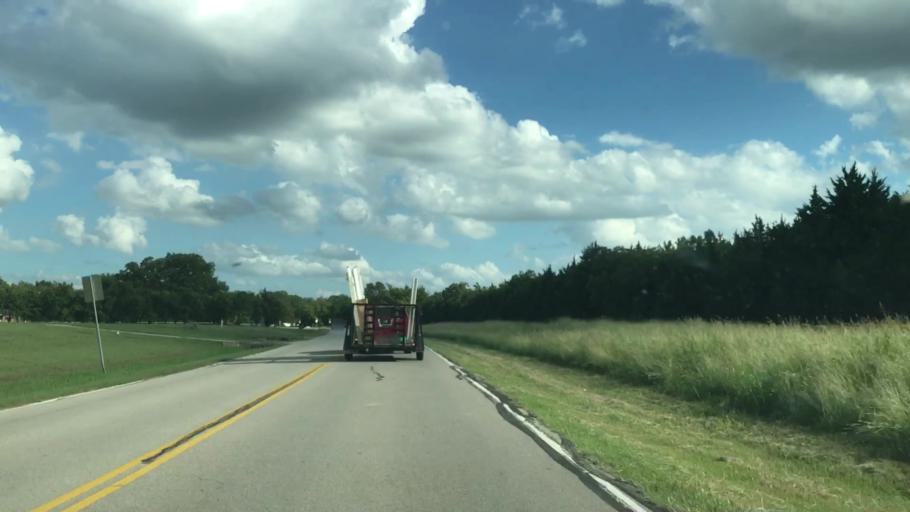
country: US
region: Texas
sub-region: Dallas County
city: Rowlett
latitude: 32.8823
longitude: -96.5254
